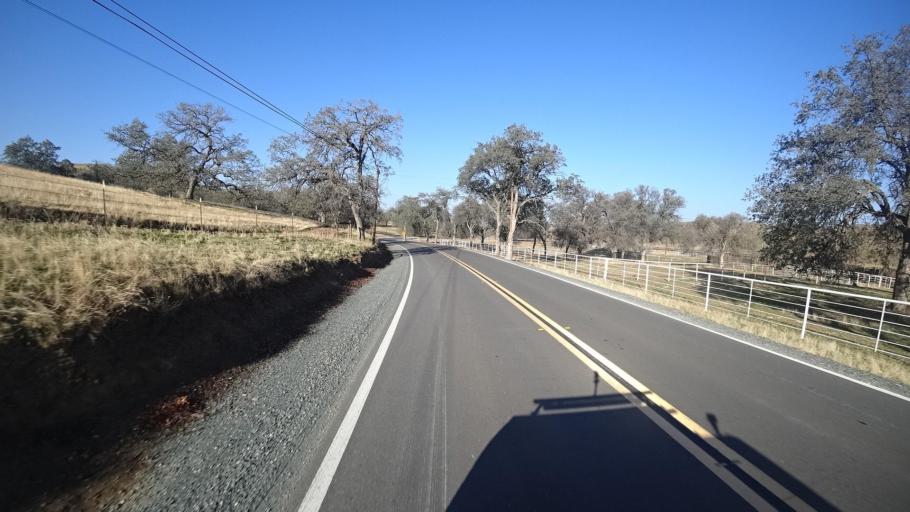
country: US
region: California
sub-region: Tulare County
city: Richgrove
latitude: 35.7136
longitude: -118.8586
